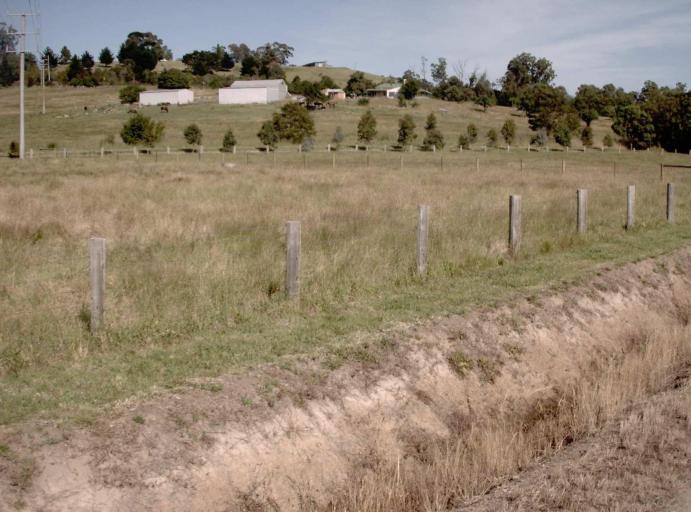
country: AU
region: Victoria
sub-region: East Gippsland
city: Bairnsdale
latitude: -37.7245
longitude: 147.8070
